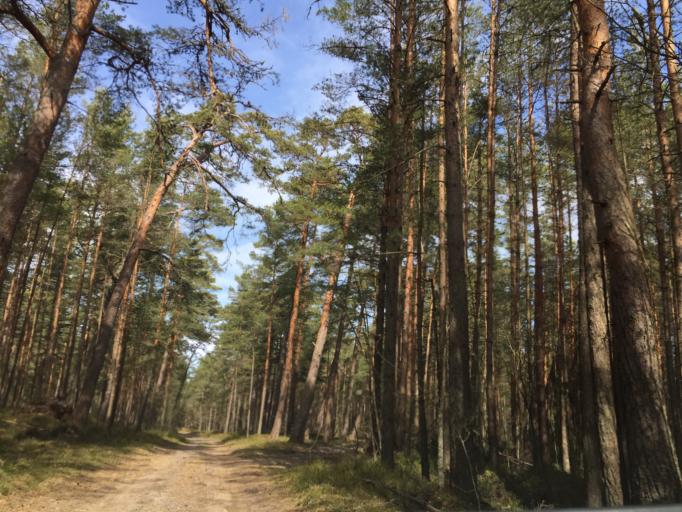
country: LV
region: Salacgrivas
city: Salacgriva
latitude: 57.6960
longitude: 24.3587
